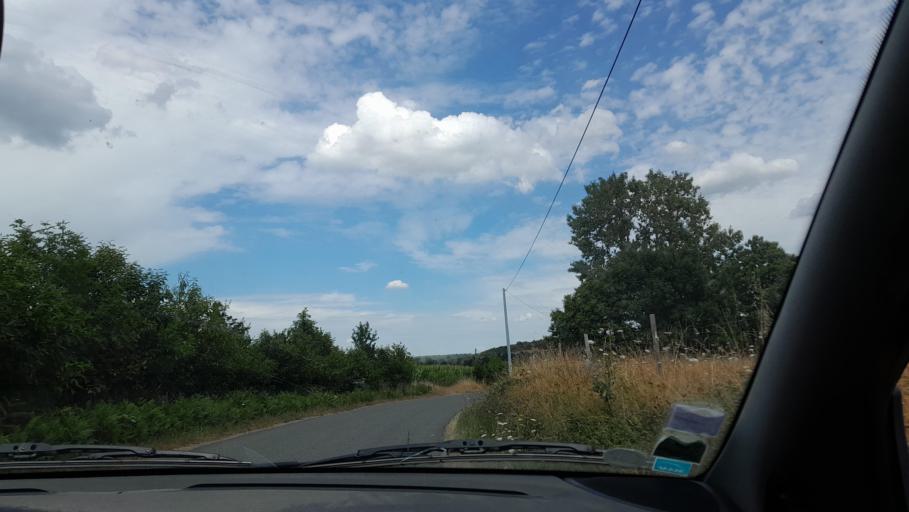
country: FR
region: Pays de la Loire
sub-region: Departement de la Mayenne
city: Juvigne
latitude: 48.1793
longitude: -1.0387
